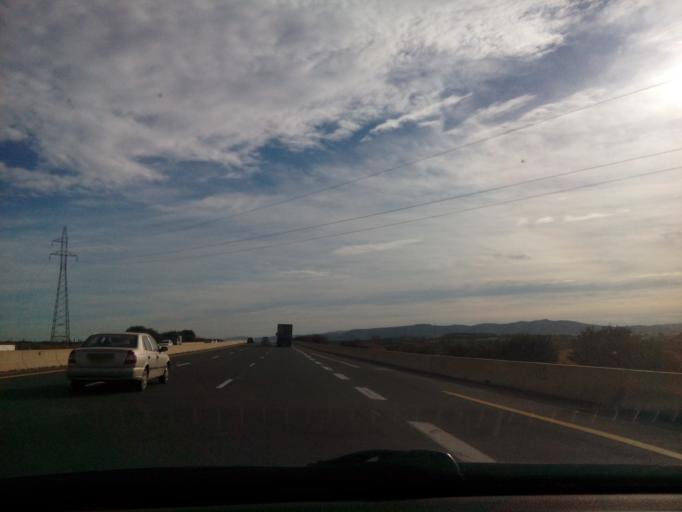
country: DZ
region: Mascara
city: Sig
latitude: 35.5428
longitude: -0.3738
